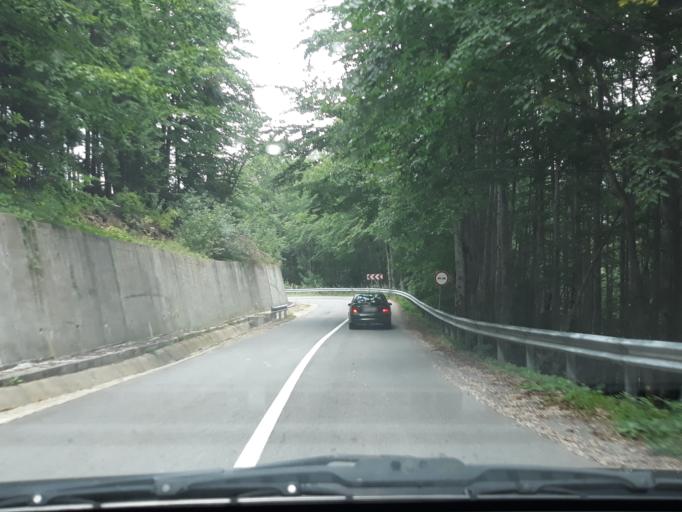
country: RO
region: Bihor
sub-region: Comuna Pietroasa
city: Pietroasa
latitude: 46.5967
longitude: 22.6722
